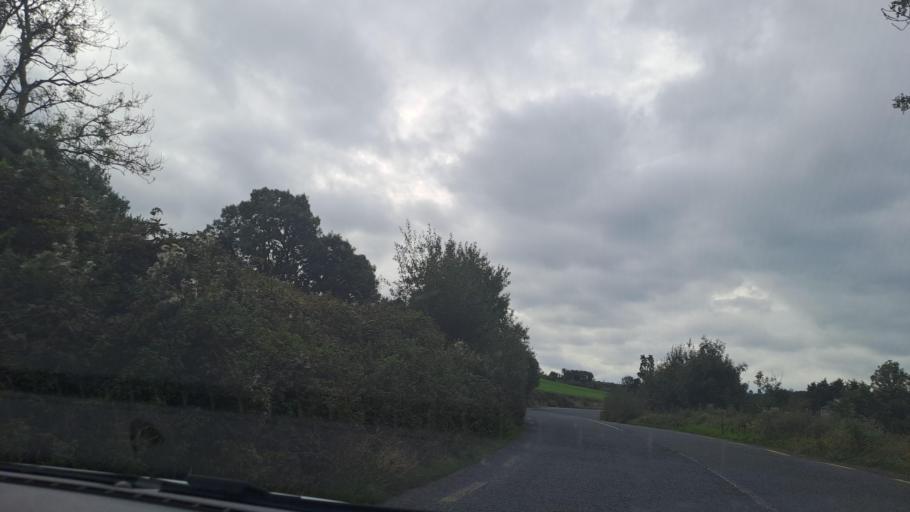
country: IE
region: Ulster
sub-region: An Cabhan
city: Bailieborough
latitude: 53.9316
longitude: -6.9216
